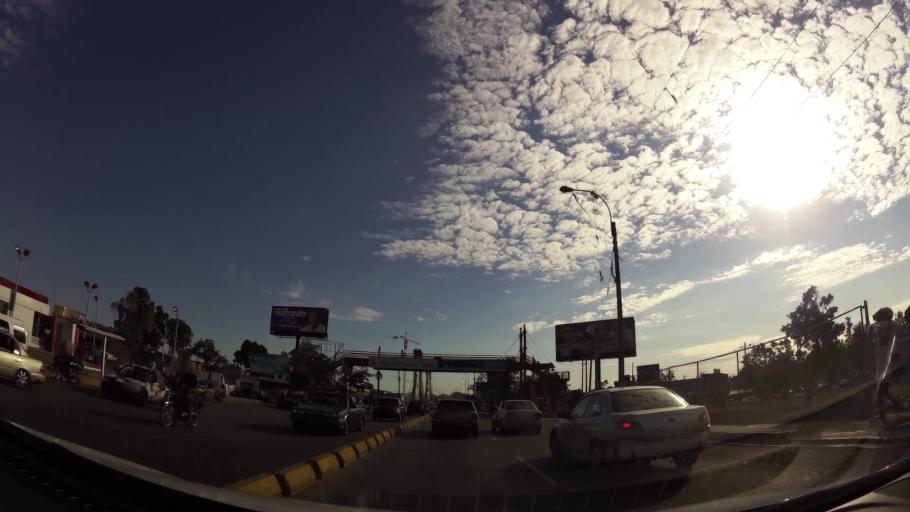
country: DO
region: Nacional
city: Ensanche Luperon
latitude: 18.5041
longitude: -69.8838
